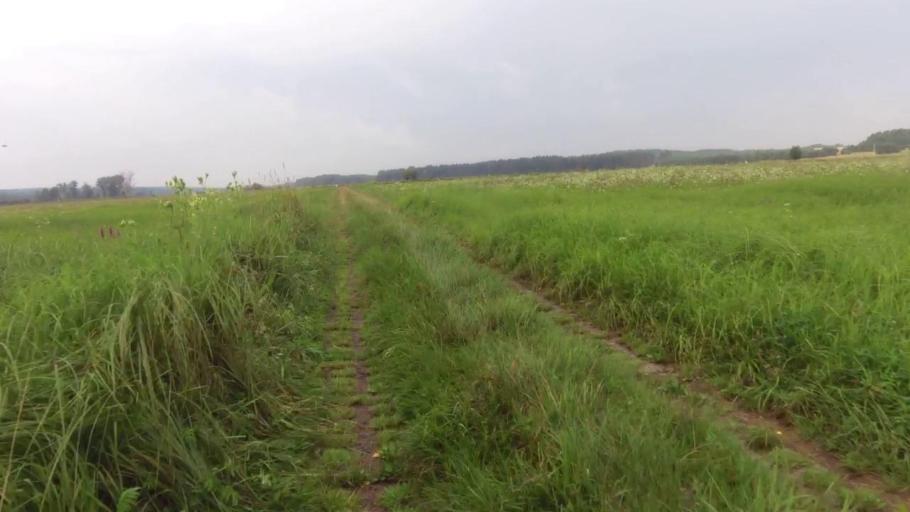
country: PL
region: West Pomeranian Voivodeship
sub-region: Powiat stargardzki
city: Suchan
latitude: 53.2515
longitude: 15.3948
